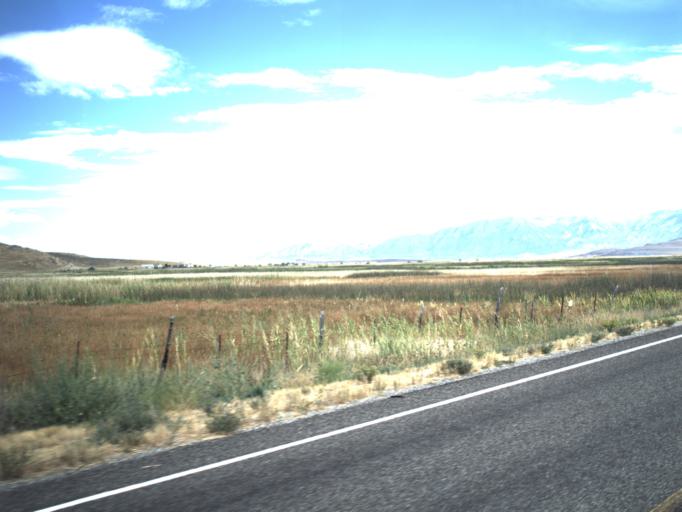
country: US
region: Utah
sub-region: Box Elder County
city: Tremonton
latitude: 41.6124
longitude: -112.3633
